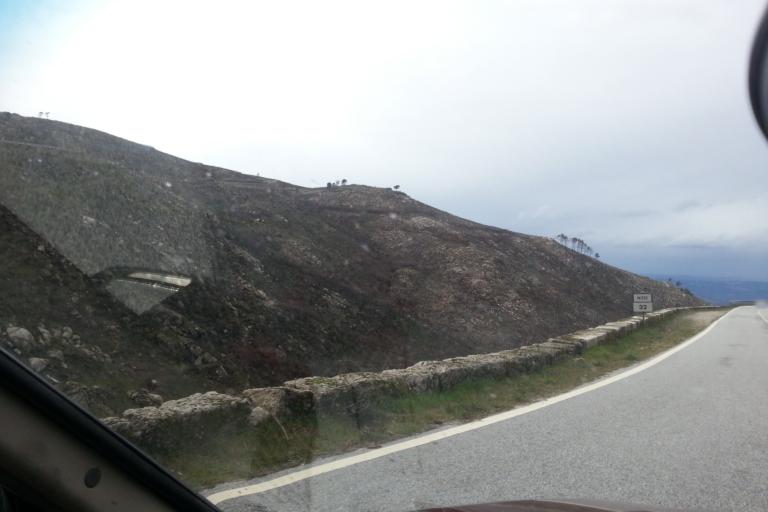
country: PT
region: Guarda
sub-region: Manteigas
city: Manteigas
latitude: 40.4537
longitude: -7.5854
